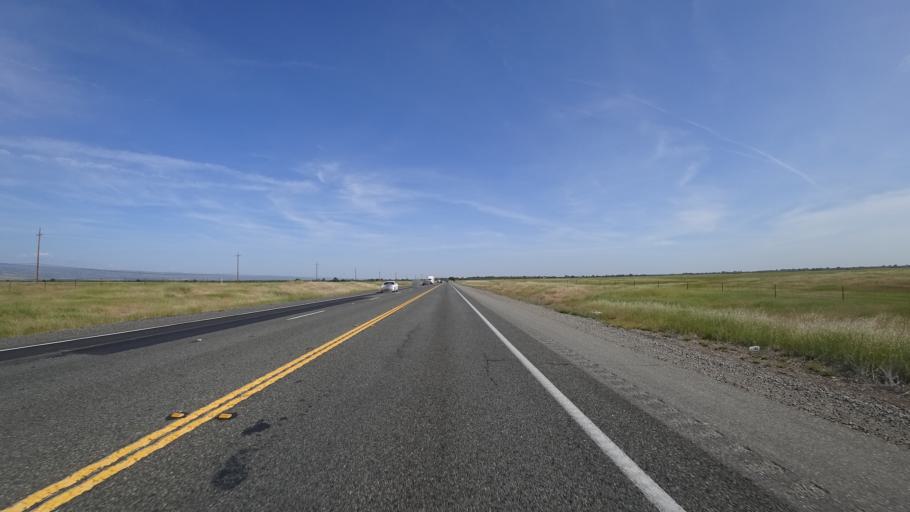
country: US
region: California
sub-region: Glenn County
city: Hamilton City
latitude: 39.8987
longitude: -121.9951
